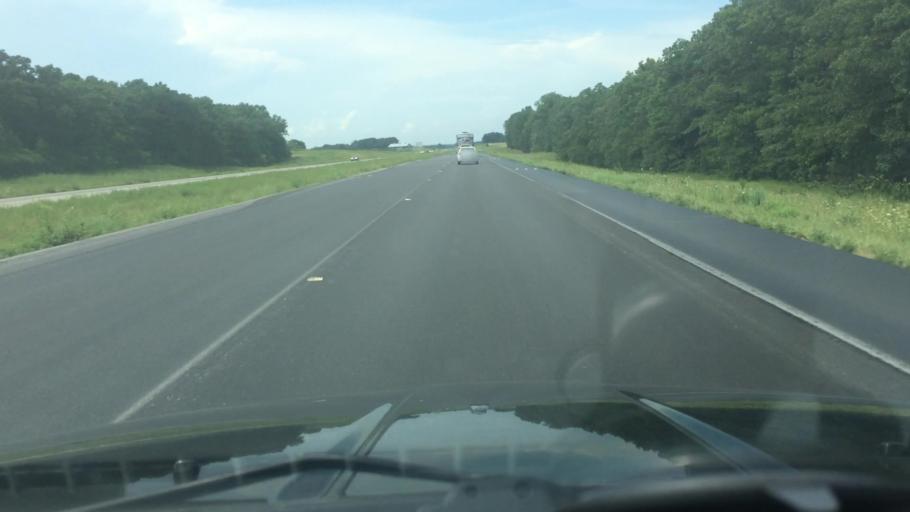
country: US
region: Missouri
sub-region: Saint Clair County
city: Osceola
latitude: 37.9692
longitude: -93.6459
